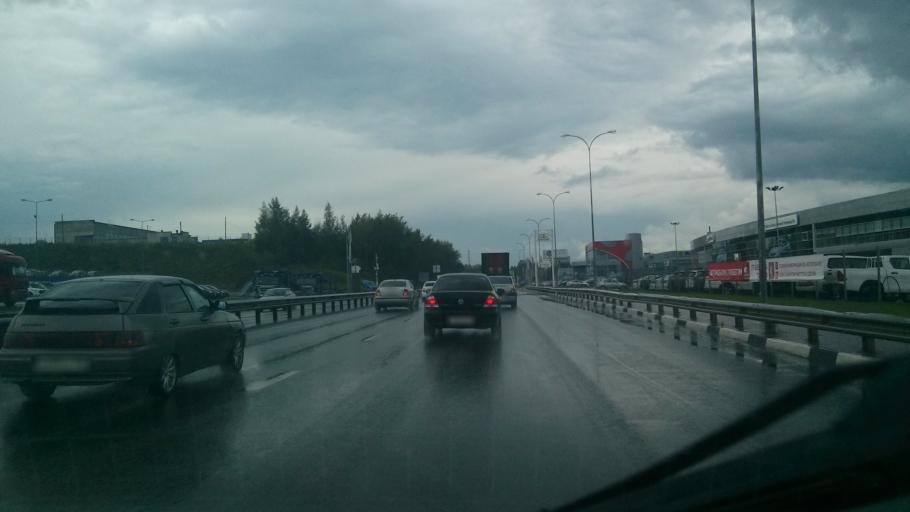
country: RU
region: Nizjnij Novgorod
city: Afonino
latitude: 56.2361
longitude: 44.0198
